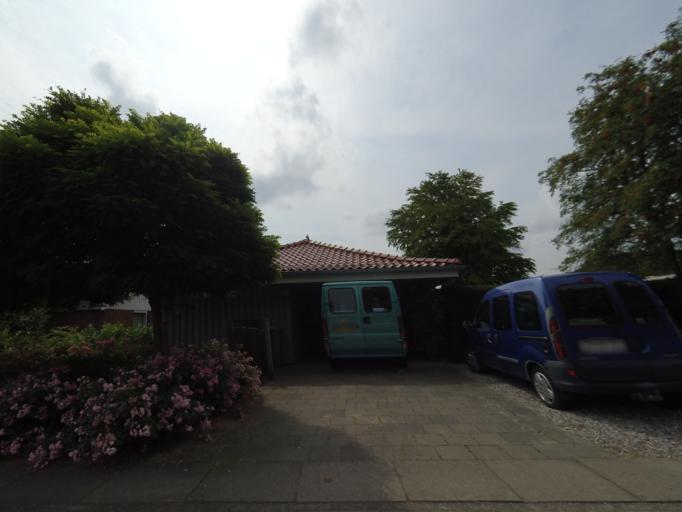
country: DK
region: South Denmark
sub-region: Odense Kommune
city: Bellinge
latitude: 55.3680
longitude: 10.3479
